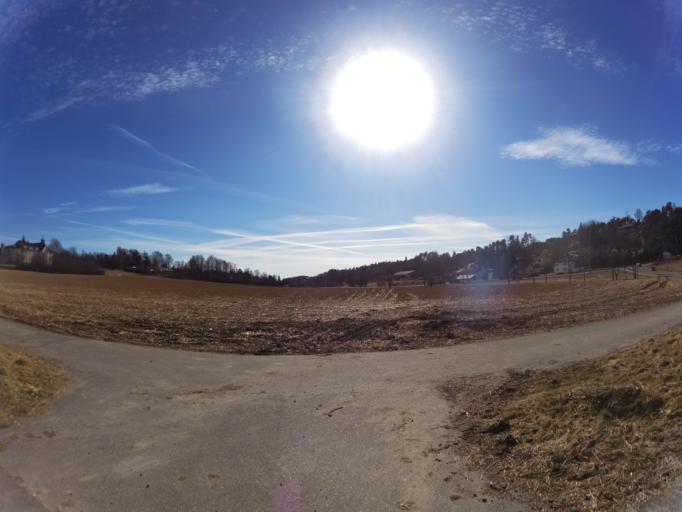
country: NO
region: Ostfold
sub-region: Fredrikstad
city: Fredrikstad
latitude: 59.2517
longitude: 10.9315
